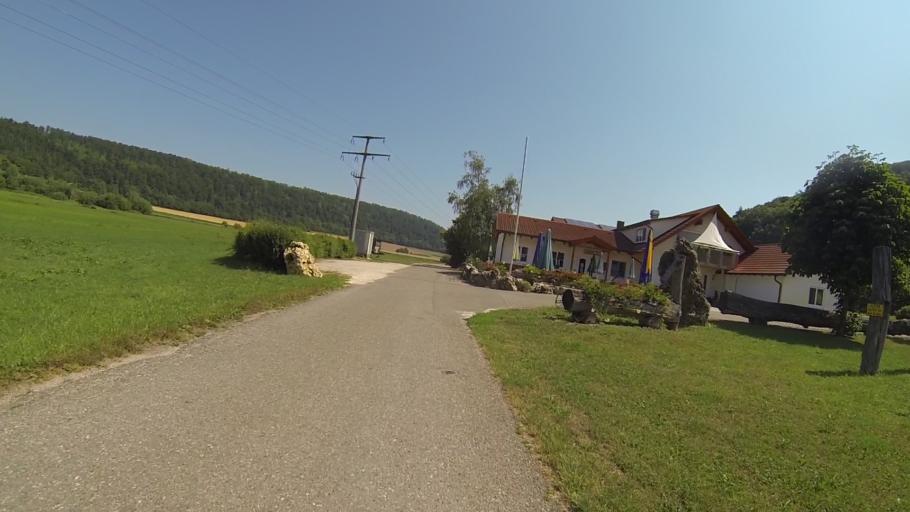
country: DE
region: Baden-Wuerttemberg
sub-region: Regierungsbezirk Stuttgart
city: Konigsbronn
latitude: 48.7296
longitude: 10.1467
